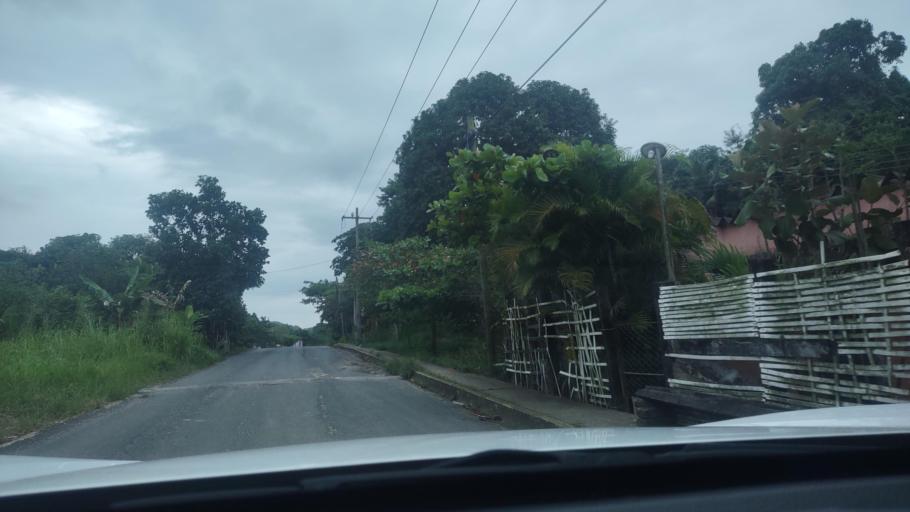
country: MX
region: Veracruz
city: Villa Nanchital
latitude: 18.0459
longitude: -94.3553
